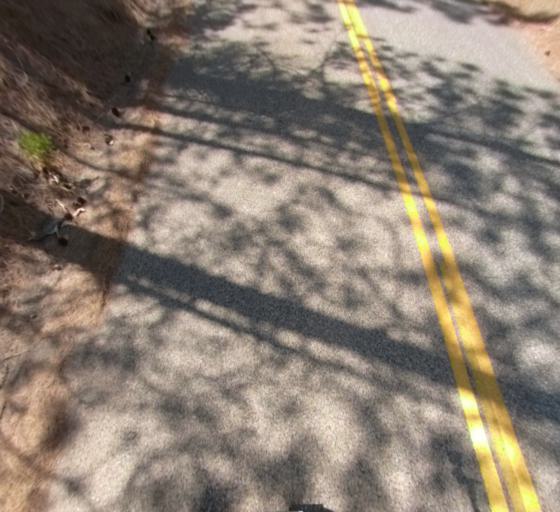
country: US
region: California
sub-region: Madera County
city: Oakhurst
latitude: 37.4065
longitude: -119.3482
